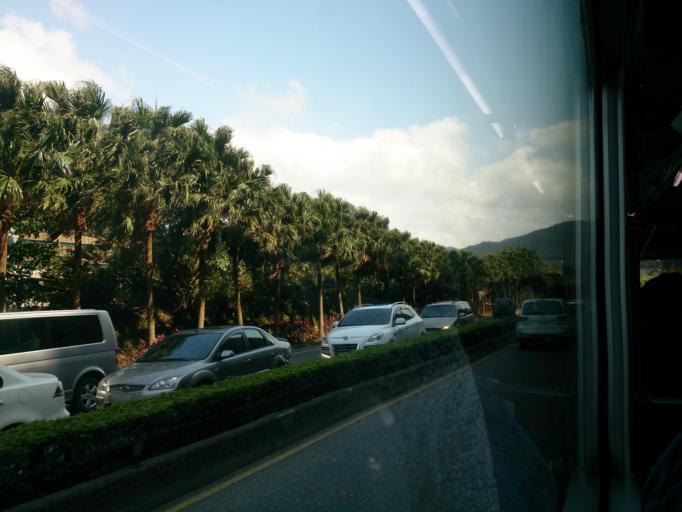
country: TW
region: Taipei
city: Taipei
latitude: 25.0017
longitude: 121.6008
